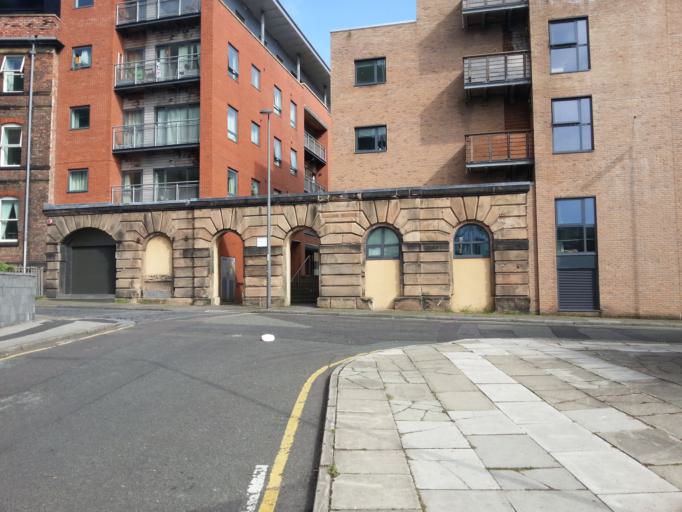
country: GB
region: England
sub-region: Liverpool
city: Liverpool
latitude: 53.4002
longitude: -2.9797
